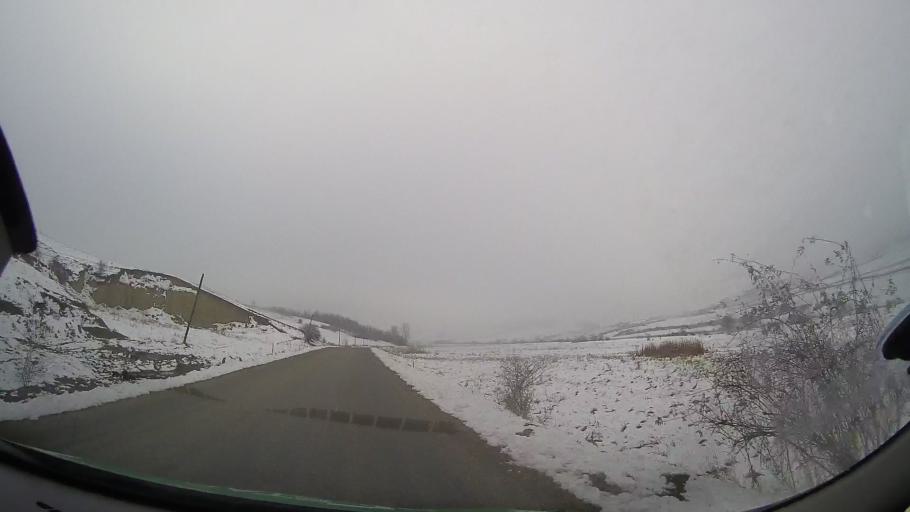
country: RO
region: Bacau
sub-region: Comuna Vultureni
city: Vultureni
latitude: 46.3153
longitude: 27.2930
